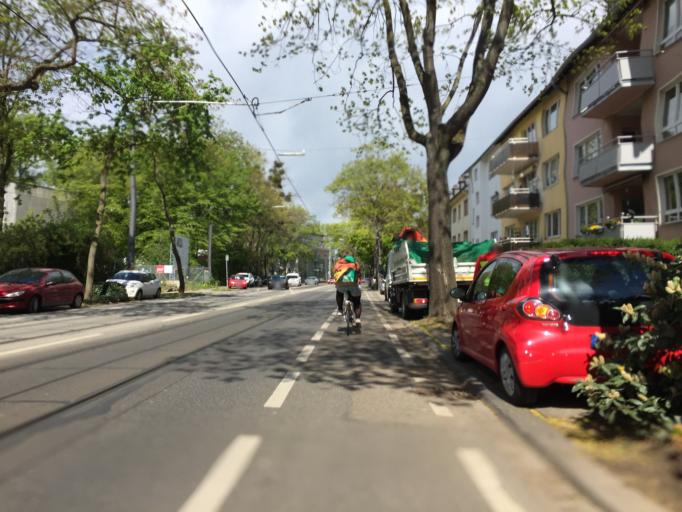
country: DE
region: North Rhine-Westphalia
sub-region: Regierungsbezirk Koln
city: Bonn
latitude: 50.7178
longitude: 7.1077
